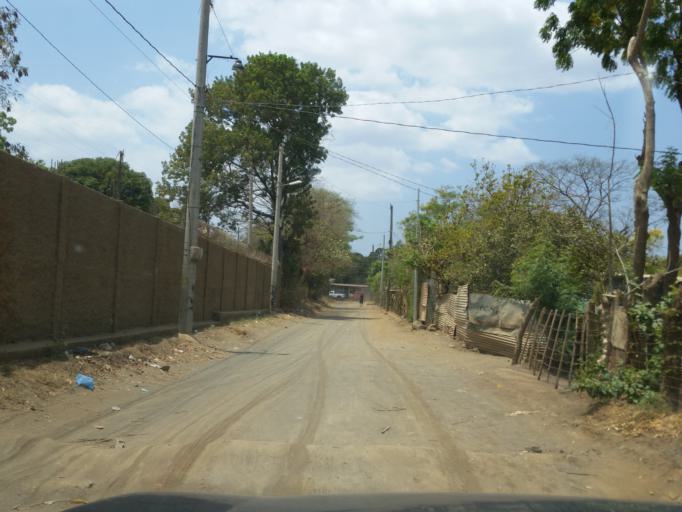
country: NI
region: Managua
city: Managua
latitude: 12.1248
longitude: -86.1920
